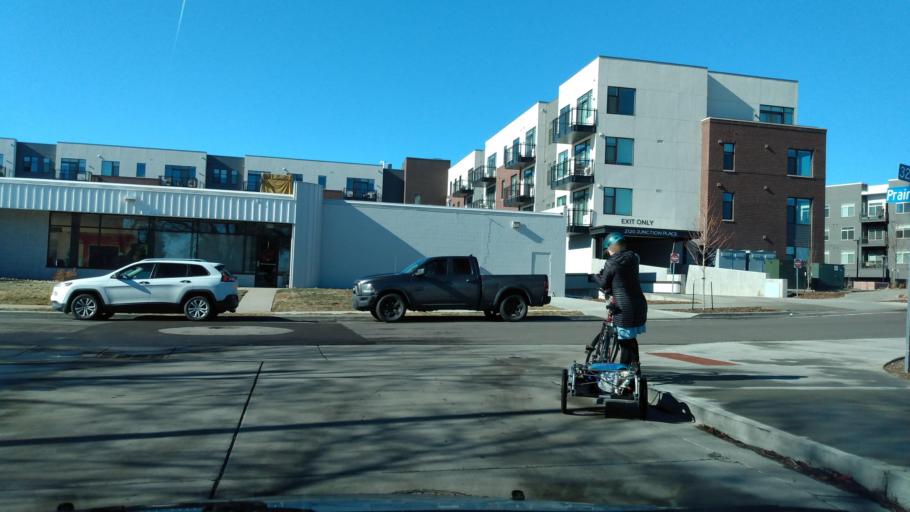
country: US
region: Colorado
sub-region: Boulder County
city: Boulder
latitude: 40.0220
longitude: -105.2513
